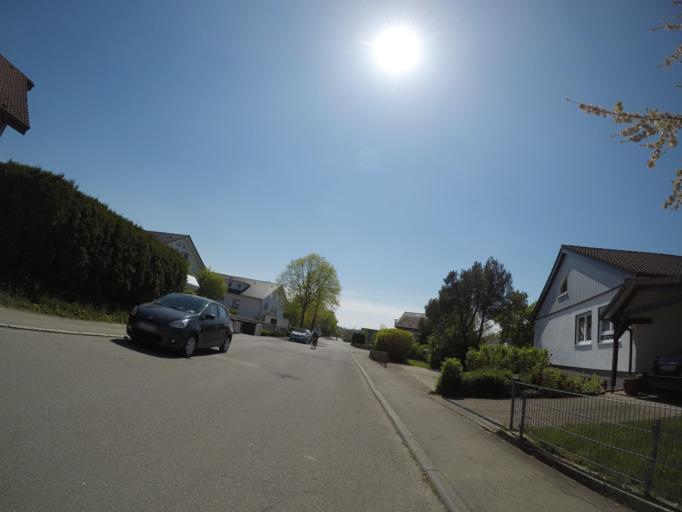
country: DE
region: Baden-Wuerttemberg
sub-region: Tuebingen Region
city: Markdorf
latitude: 47.7145
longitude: 9.3884
